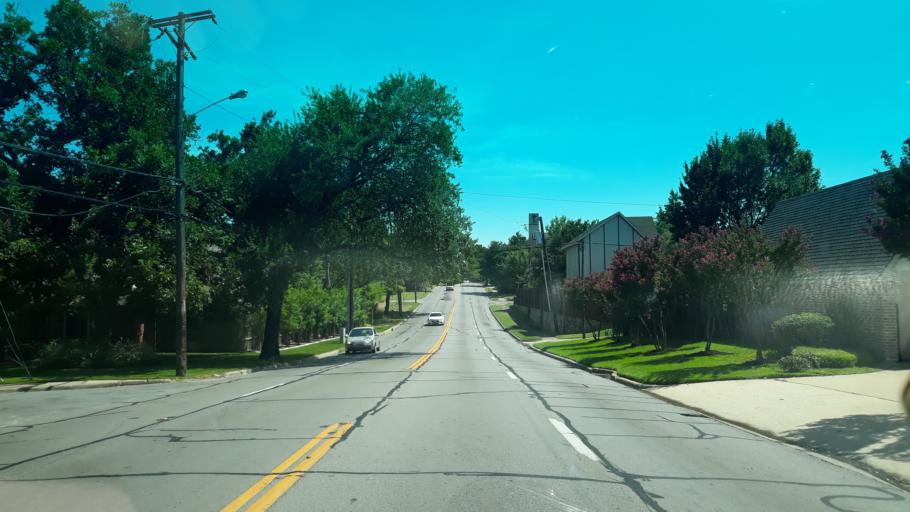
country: US
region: Texas
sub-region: Dallas County
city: Highland Park
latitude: 32.8242
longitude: -96.7529
